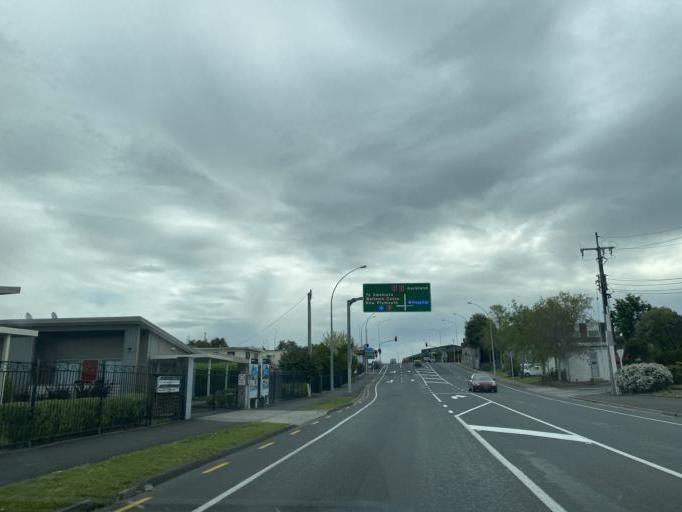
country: NZ
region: Waikato
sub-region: Hamilton City
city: Hamilton
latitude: -37.8077
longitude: 175.2822
